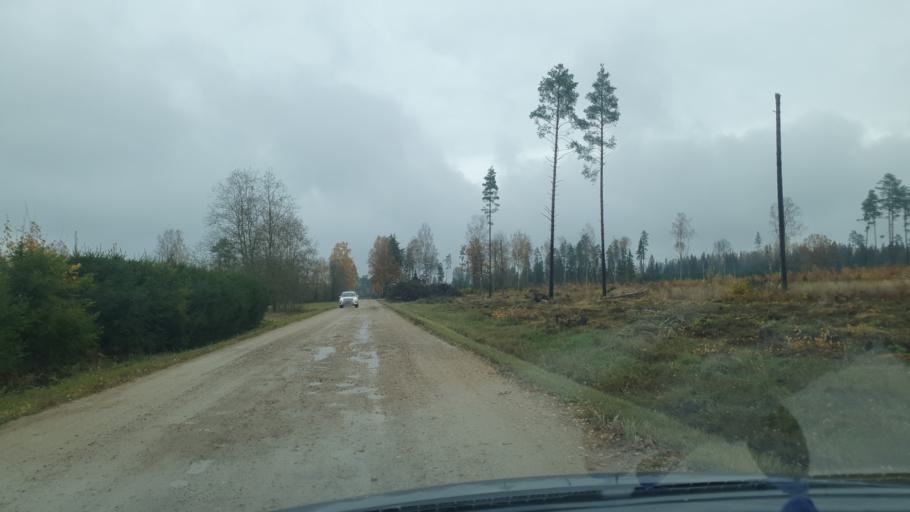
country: EE
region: Viljandimaa
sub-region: Karksi vald
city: Karksi-Nuia
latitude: 58.0090
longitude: 25.6575
